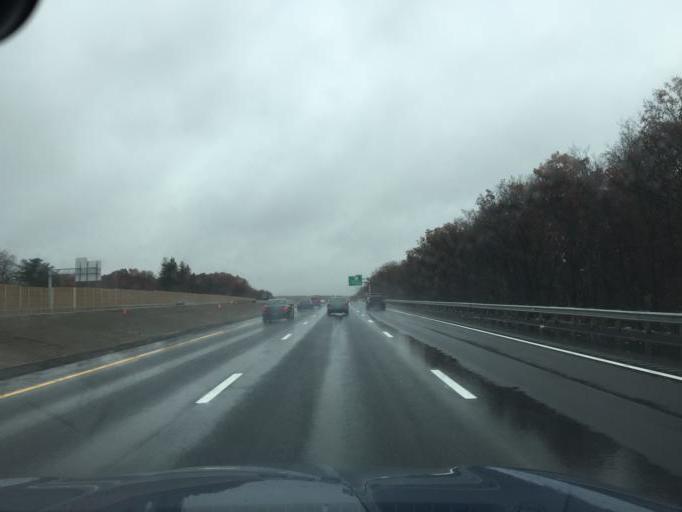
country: US
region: Massachusetts
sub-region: Bristol County
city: Attleboro
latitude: 41.9602
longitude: -71.3006
